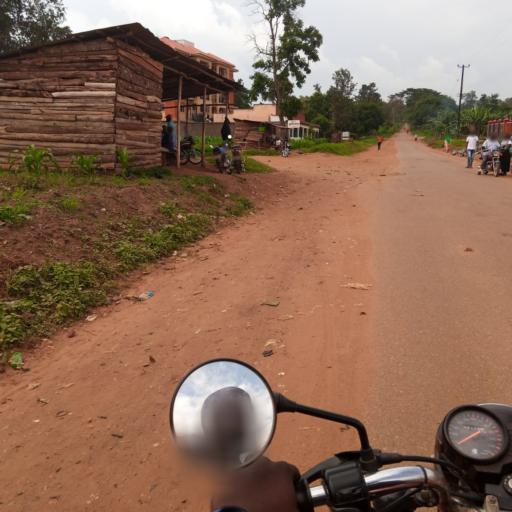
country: UG
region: Eastern Region
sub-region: Mbale District
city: Mbale
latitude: 1.0886
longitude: 34.1842
